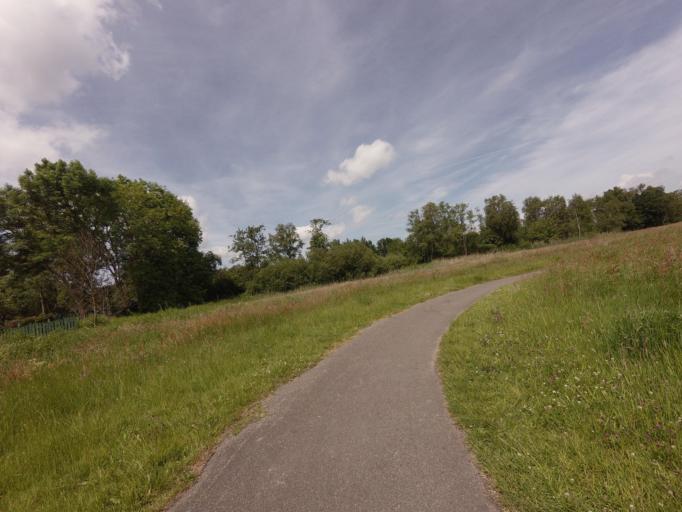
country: NL
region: Utrecht
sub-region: Gemeente Utrecht
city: Utrecht
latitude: 52.1307
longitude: 5.1314
